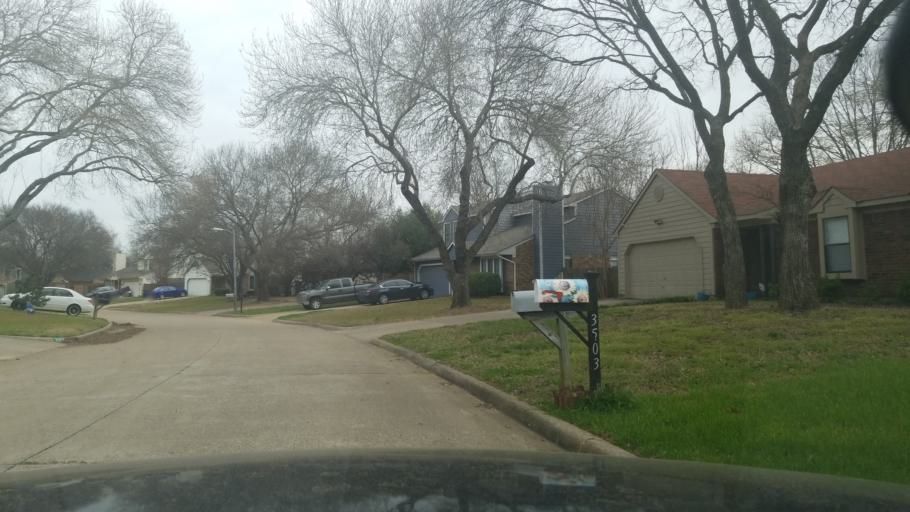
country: US
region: Texas
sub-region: Denton County
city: Hickory Creek
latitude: 33.1342
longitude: -97.0500
